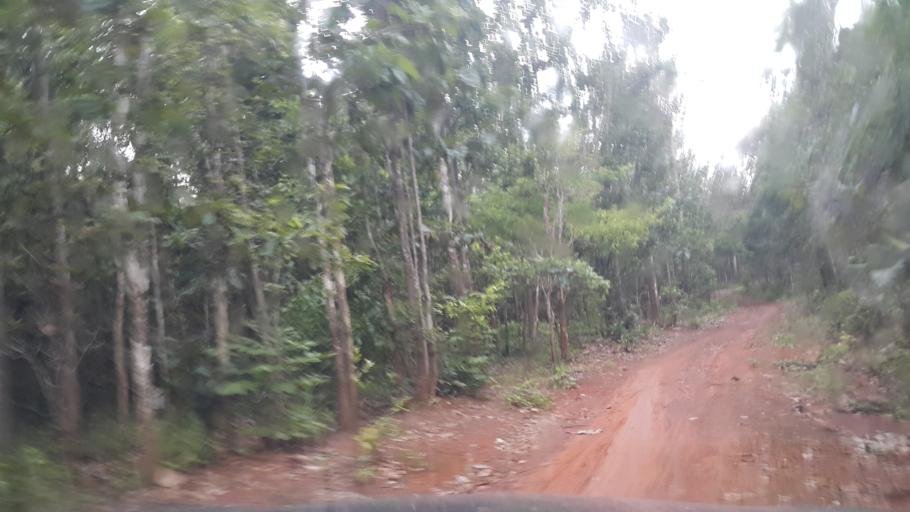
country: TH
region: Chiang Mai
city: San Sai
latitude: 18.9948
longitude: 99.1325
